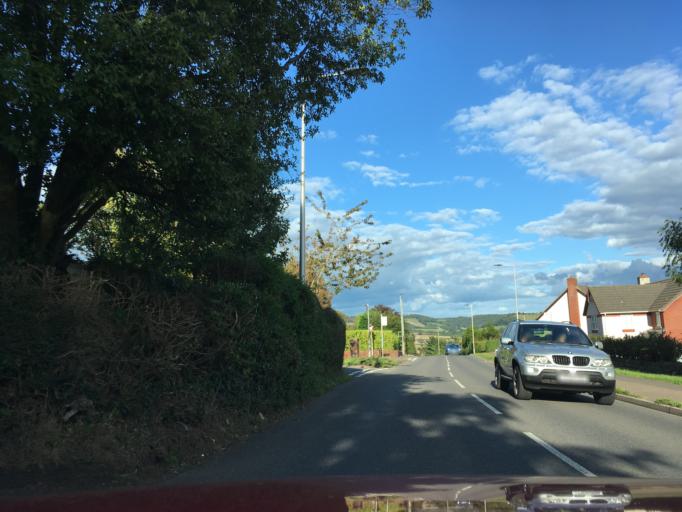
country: GB
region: England
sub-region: Devon
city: Sidmouth
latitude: 50.7017
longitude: -3.2383
